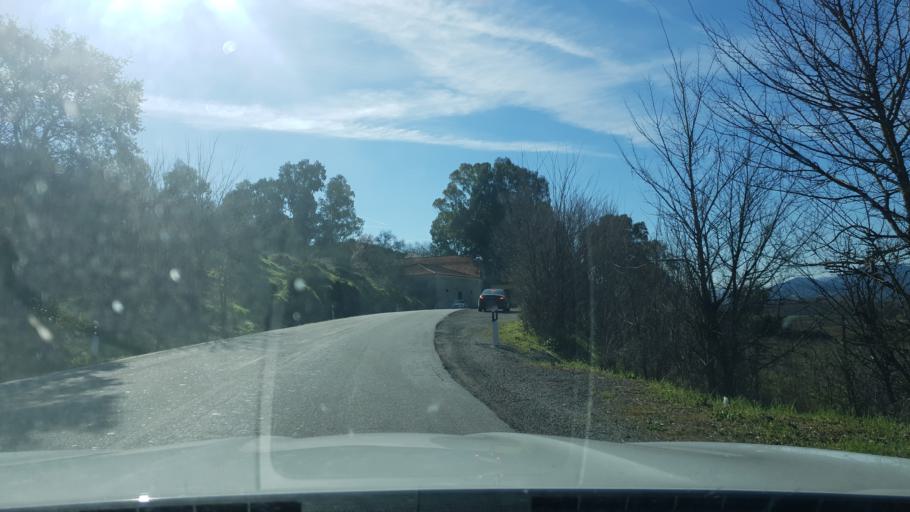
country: PT
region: Braganca
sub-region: Torre de Moncorvo
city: Torre de Moncorvo
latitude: 41.2182
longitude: -7.0919
